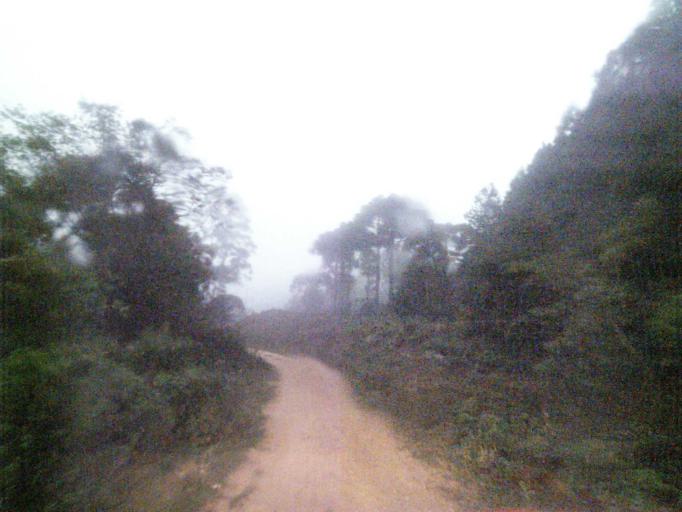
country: BR
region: Santa Catarina
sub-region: Anitapolis
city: Anitapolis
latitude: -27.7887
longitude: -49.1373
